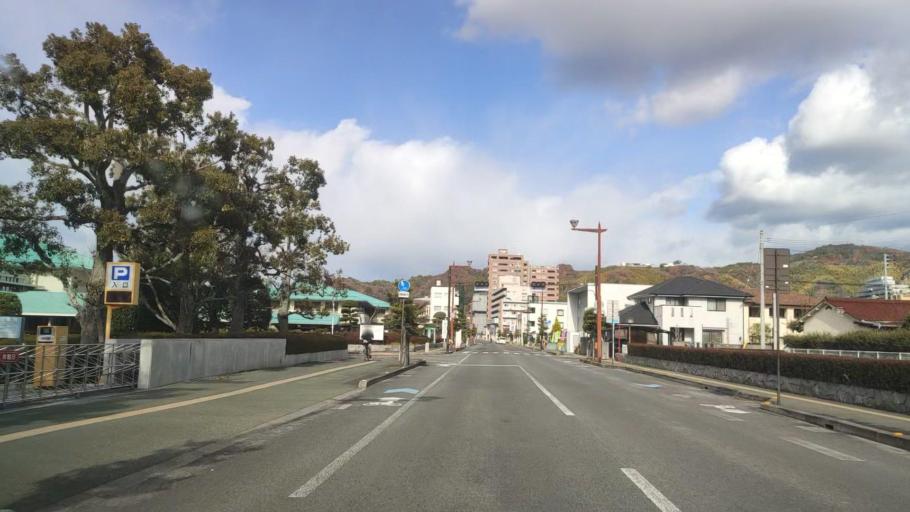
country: JP
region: Ehime
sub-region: Shikoku-chuo Shi
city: Matsuyama
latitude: 33.8490
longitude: 132.7806
